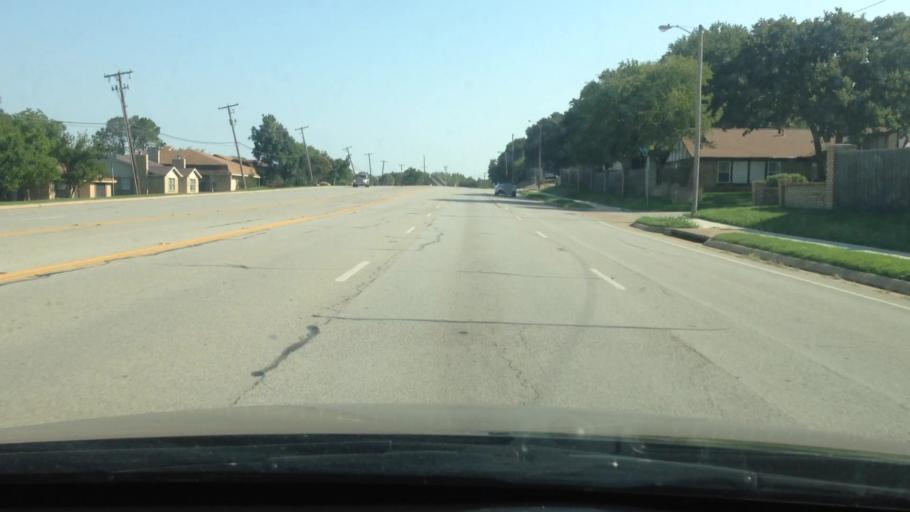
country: US
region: Texas
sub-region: Tarrant County
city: Colleyville
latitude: 32.8825
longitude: -97.2036
